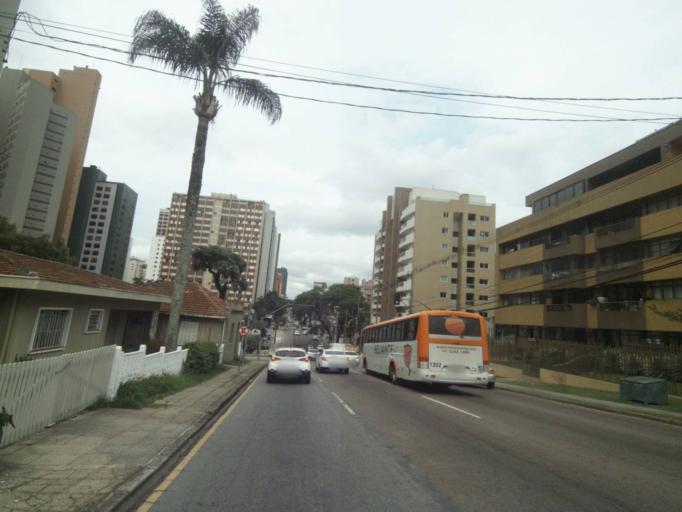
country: BR
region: Parana
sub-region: Curitiba
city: Curitiba
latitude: -25.4339
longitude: -49.2989
